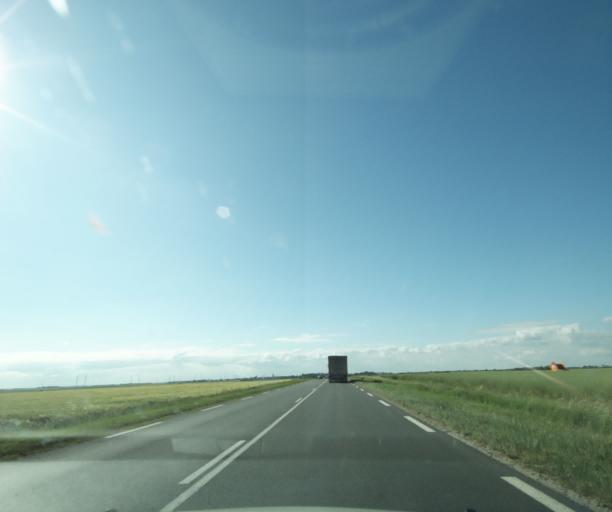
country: FR
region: Centre
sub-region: Departement d'Eure-et-Loir
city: Janville
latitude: 48.2475
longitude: 1.7720
